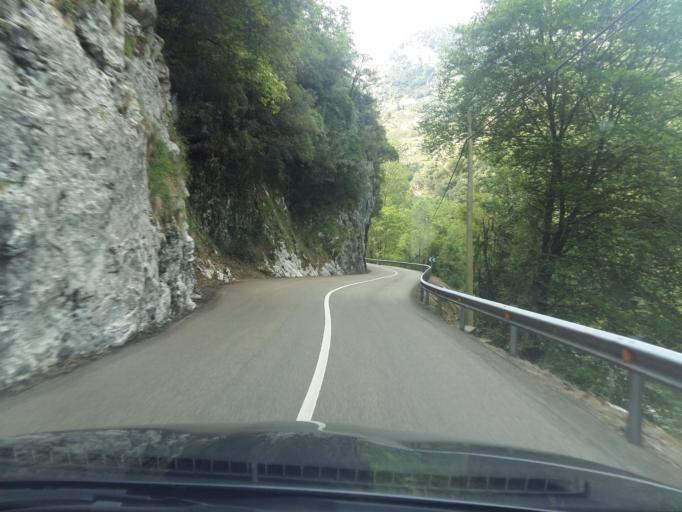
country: ES
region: Cantabria
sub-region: Provincia de Cantabria
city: Tresviso
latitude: 43.3135
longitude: -4.6088
